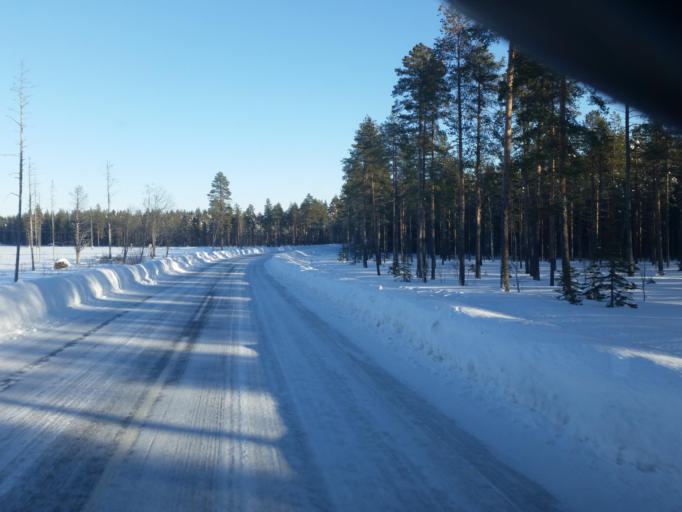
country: SE
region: Norrbotten
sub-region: Pitea Kommun
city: Roknas
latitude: 65.3491
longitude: 21.0158
